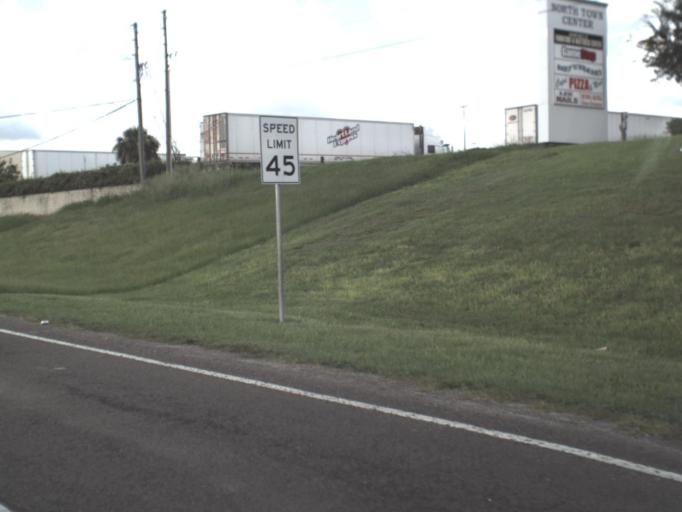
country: US
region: Florida
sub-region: Pasco County
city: Zephyrhills North
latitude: 28.2716
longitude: -82.1883
